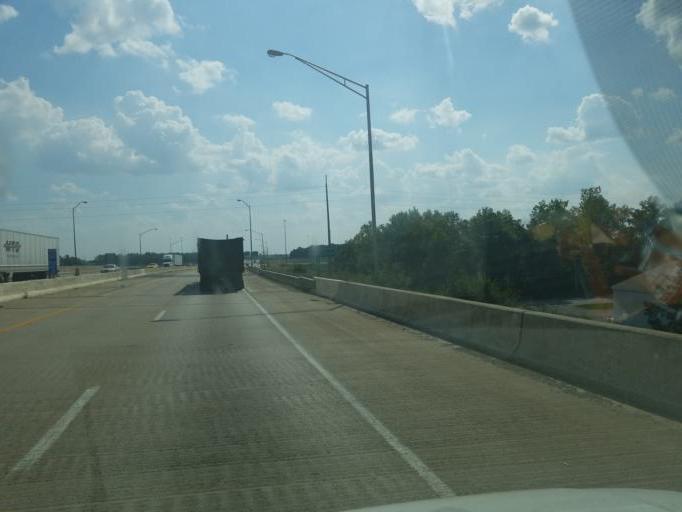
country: US
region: Indiana
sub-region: Allen County
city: New Haven
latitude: 41.0716
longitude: -84.9900
